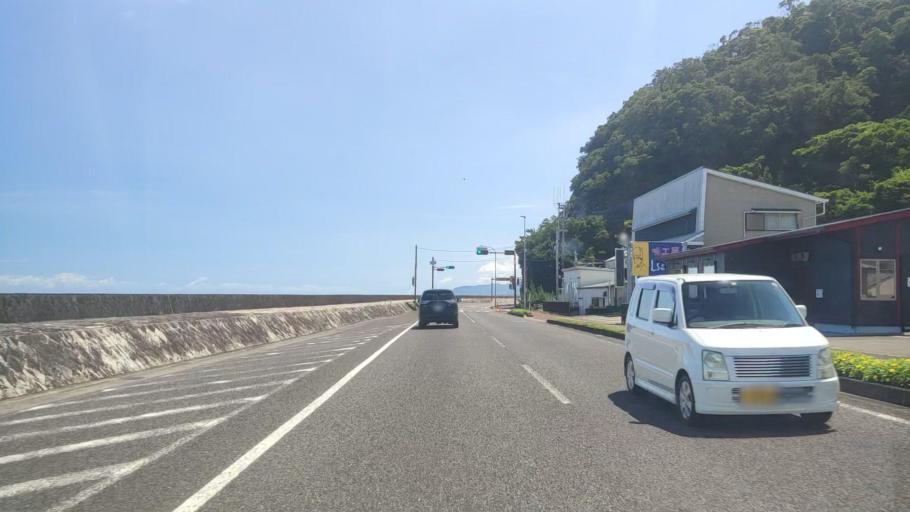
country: JP
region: Wakayama
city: Shingu
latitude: 33.8805
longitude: 136.0945
